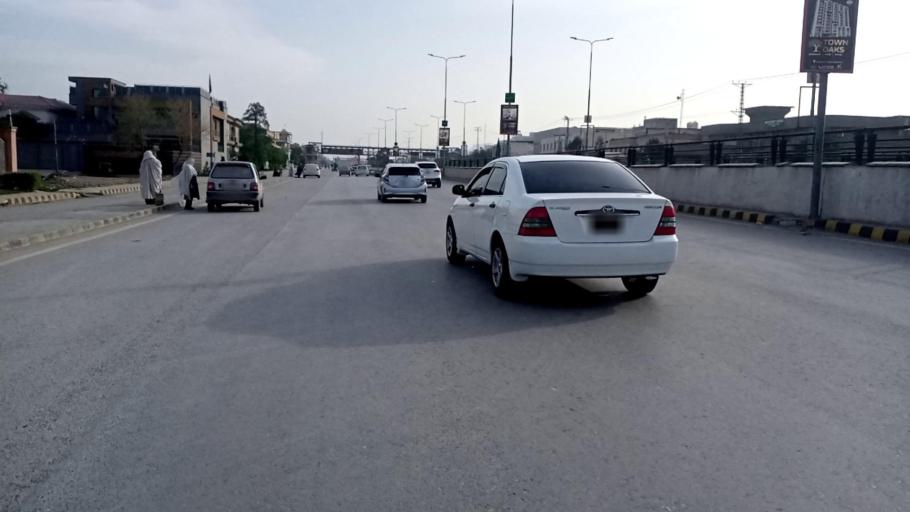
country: PK
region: Khyber Pakhtunkhwa
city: Peshawar
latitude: 33.9924
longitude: 71.4435
